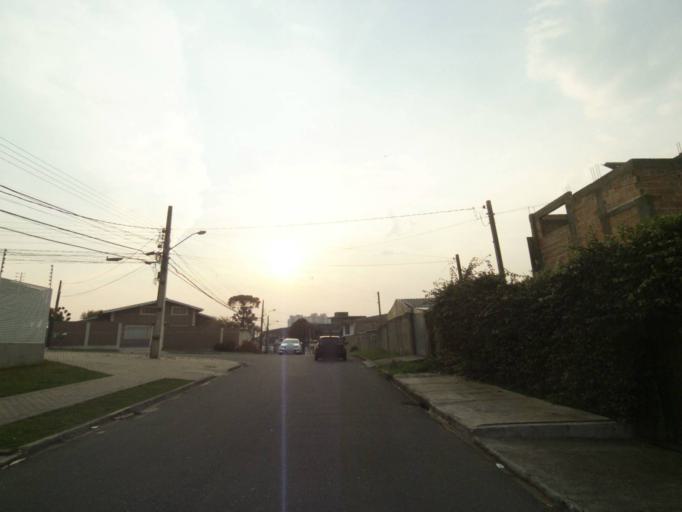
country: BR
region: Parana
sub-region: Curitiba
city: Curitiba
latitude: -25.4752
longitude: -49.2826
